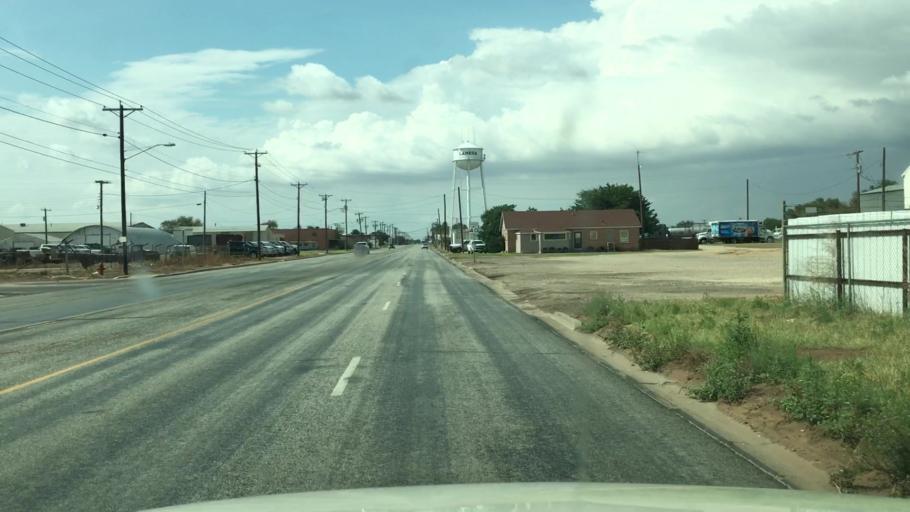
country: US
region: Texas
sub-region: Dawson County
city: Lamesa
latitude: 32.7274
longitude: -101.9474
